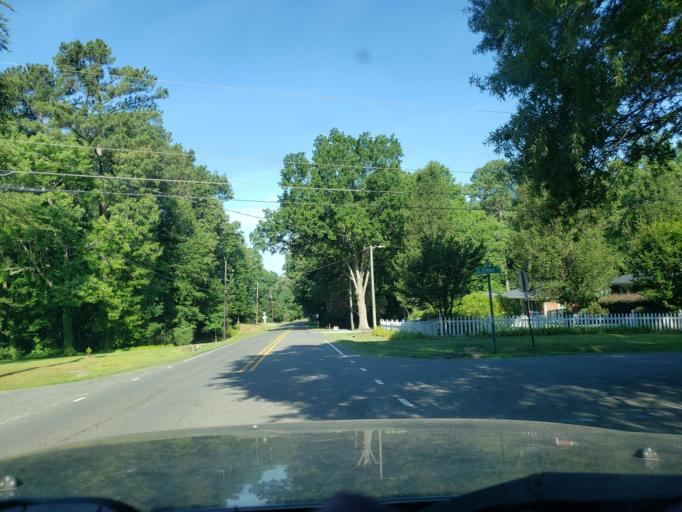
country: US
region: North Carolina
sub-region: Durham County
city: Durham
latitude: 35.9560
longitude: -78.8591
